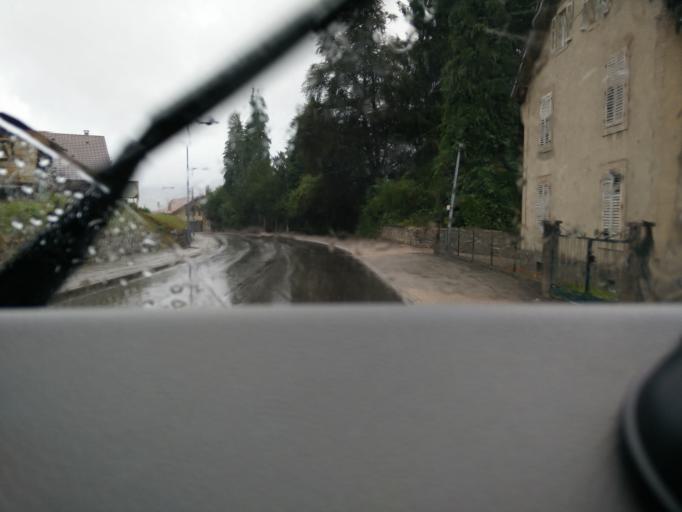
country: FR
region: Lorraine
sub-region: Departement des Vosges
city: Plainfaing
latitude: 48.1752
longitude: 7.0117
